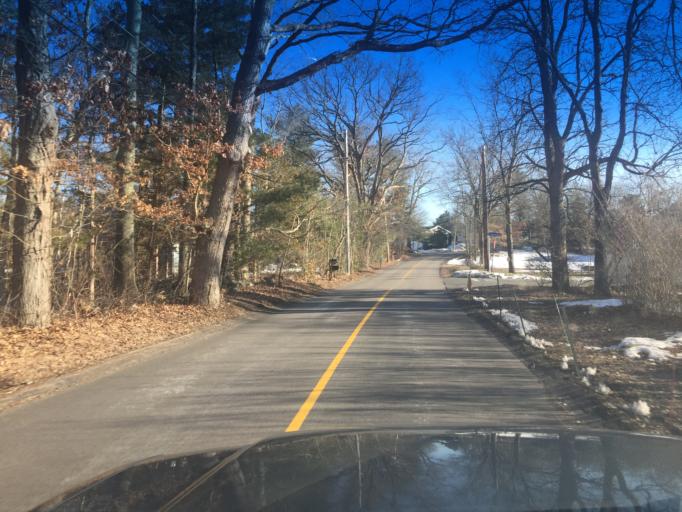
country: US
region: Massachusetts
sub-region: Norfolk County
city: Medway
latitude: 42.1448
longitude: -71.4535
